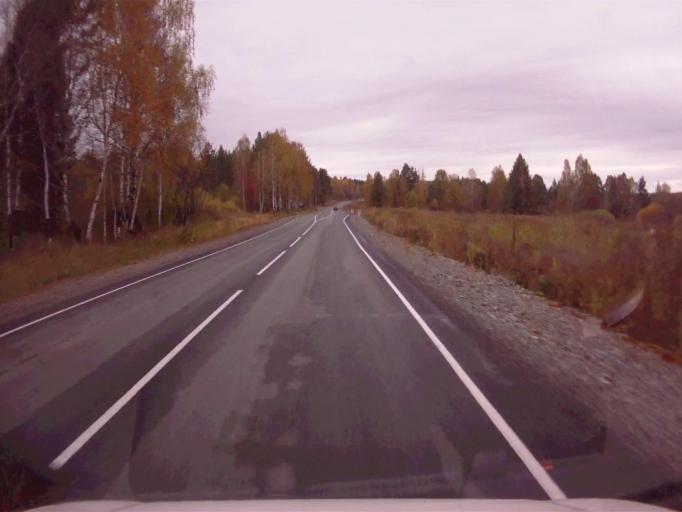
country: RU
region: Chelyabinsk
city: Nyazepetrovsk
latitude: 56.0445
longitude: 59.7658
